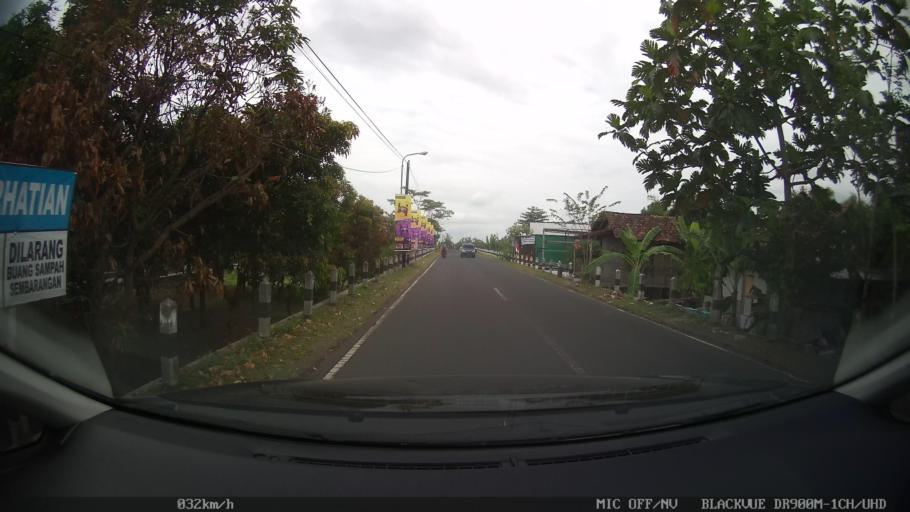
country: ID
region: Daerah Istimewa Yogyakarta
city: Depok
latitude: -7.8279
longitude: 110.4225
